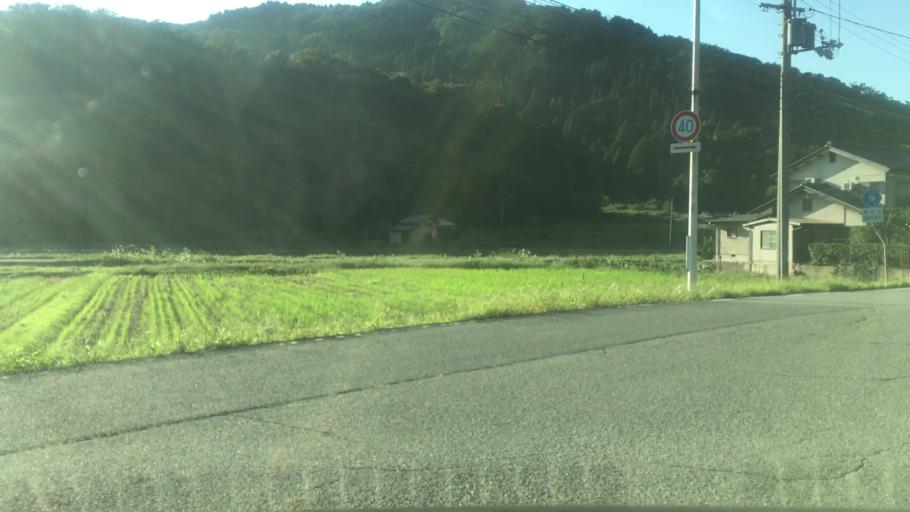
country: JP
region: Hyogo
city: Toyooka
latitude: 35.6112
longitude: 134.8290
